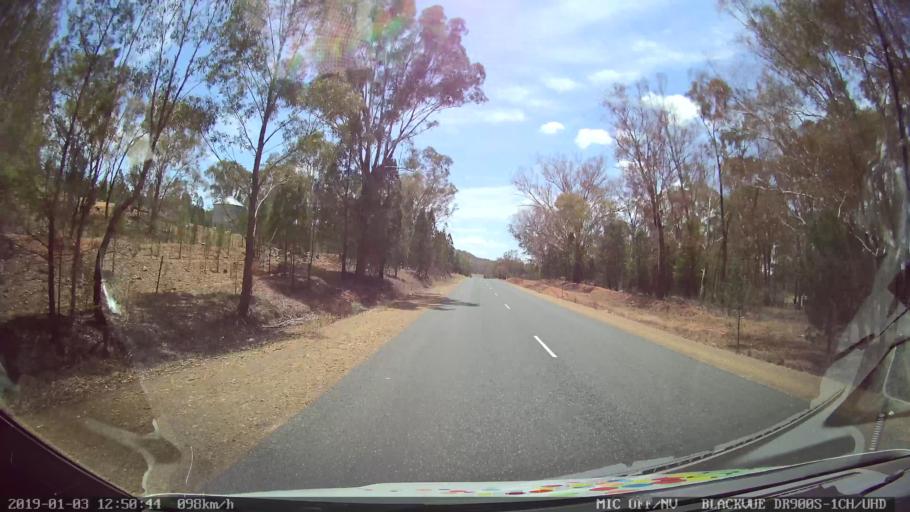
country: AU
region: New South Wales
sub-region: Weddin
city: Grenfell
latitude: -33.6881
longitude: 148.2732
